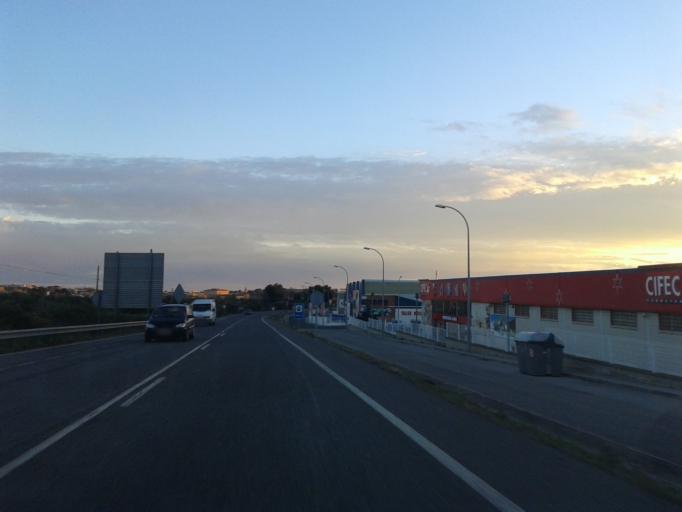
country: ES
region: Catalonia
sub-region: Provincia de Tarragona
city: Torredembarra
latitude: 41.1569
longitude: 1.3927
